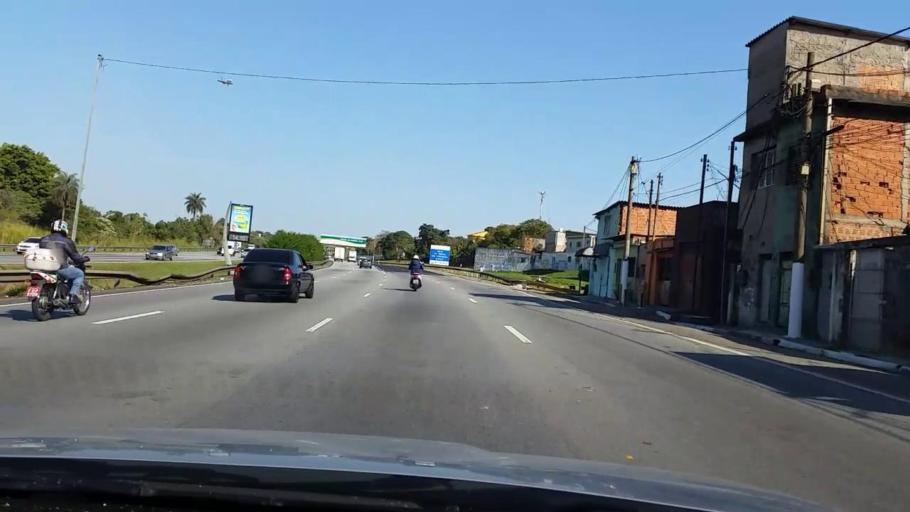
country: BR
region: Sao Paulo
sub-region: Diadema
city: Diadema
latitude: -23.6532
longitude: -46.6343
